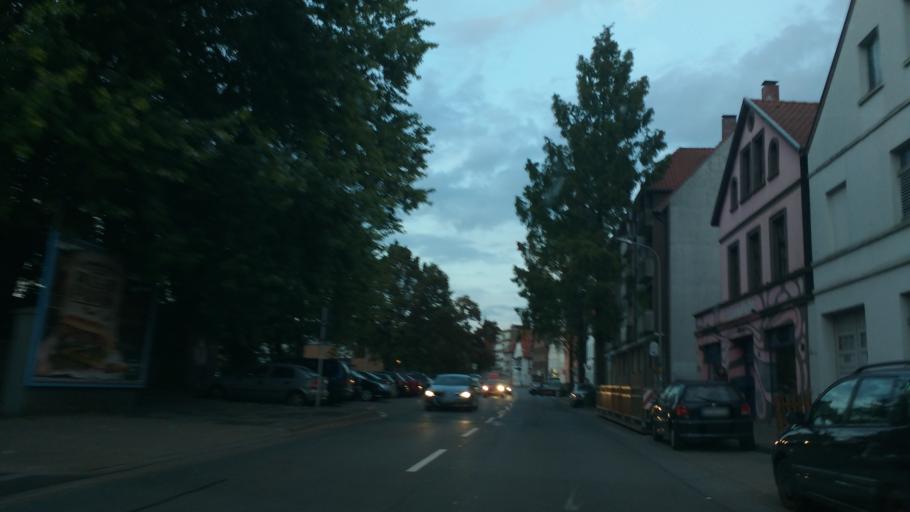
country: DE
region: North Rhine-Westphalia
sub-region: Regierungsbezirk Detmold
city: Minden
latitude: 52.2876
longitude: 8.9099
